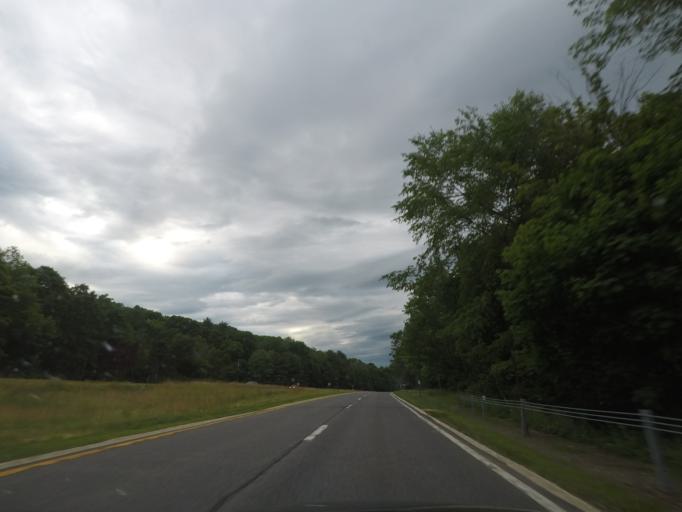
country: US
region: New York
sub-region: Dutchess County
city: Pine Plains
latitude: 42.0231
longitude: -73.7332
